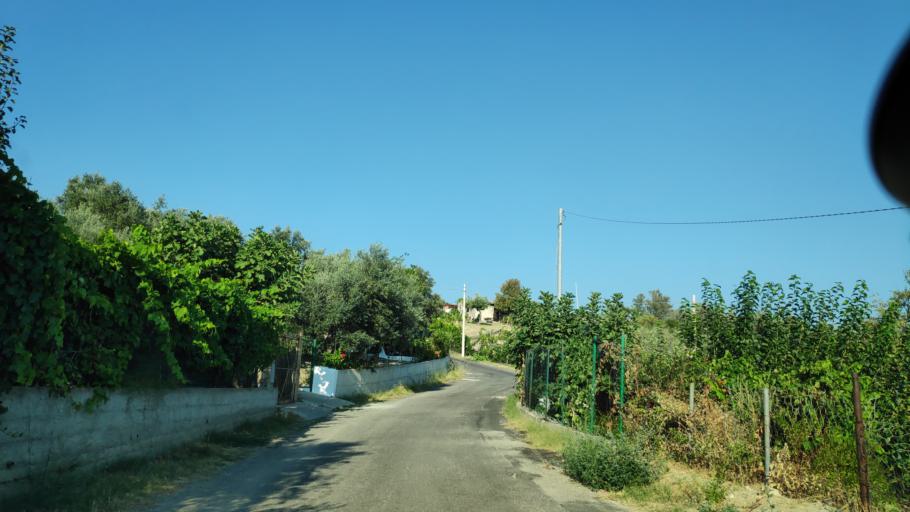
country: IT
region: Calabria
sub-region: Provincia di Catanzaro
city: Guardavalle
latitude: 38.5088
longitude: 16.5036
